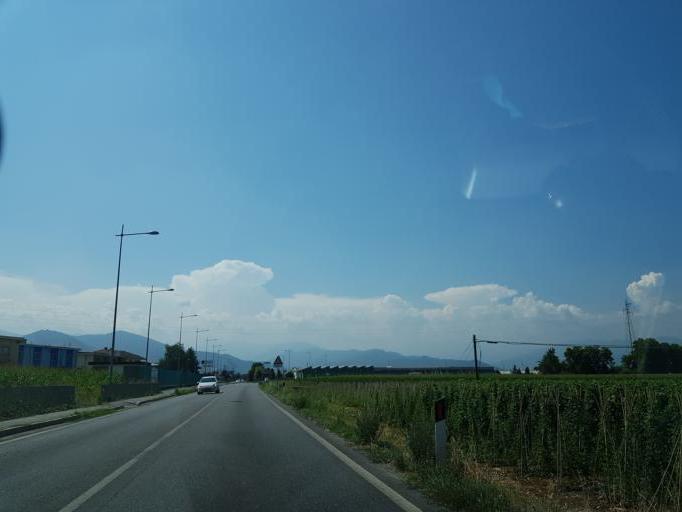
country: IT
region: Piedmont
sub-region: Provincia di Cuneo
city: San Defendente
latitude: 44.3950
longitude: 7.5003
